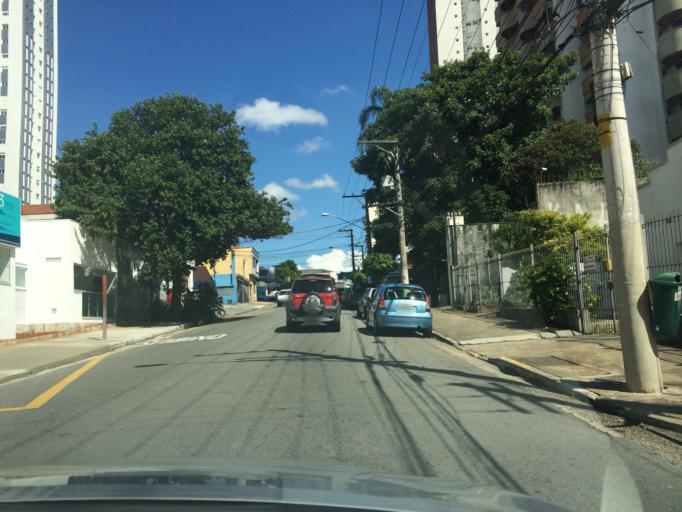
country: BR
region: Sao Paulo
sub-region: Sao Caetano Do Sul
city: Sao Caetano do Sul
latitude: -23.5519
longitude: -46.5541
